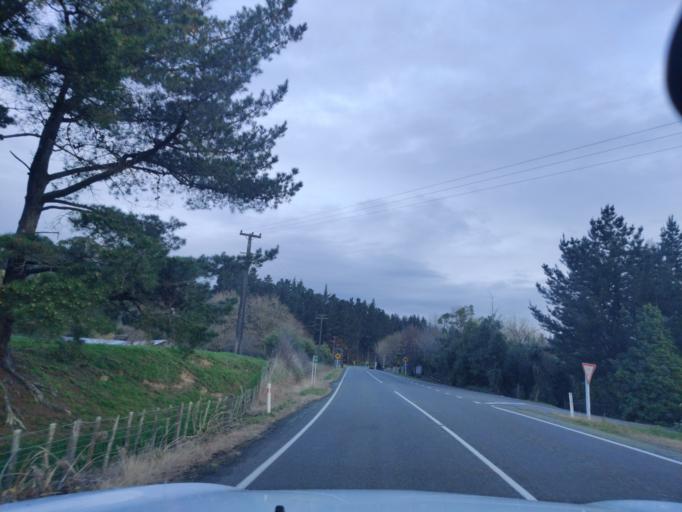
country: NZ
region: Manawatu-Wanganui
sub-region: Palmerston North City
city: Palmerston North
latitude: -40.3651
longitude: 175.6639
